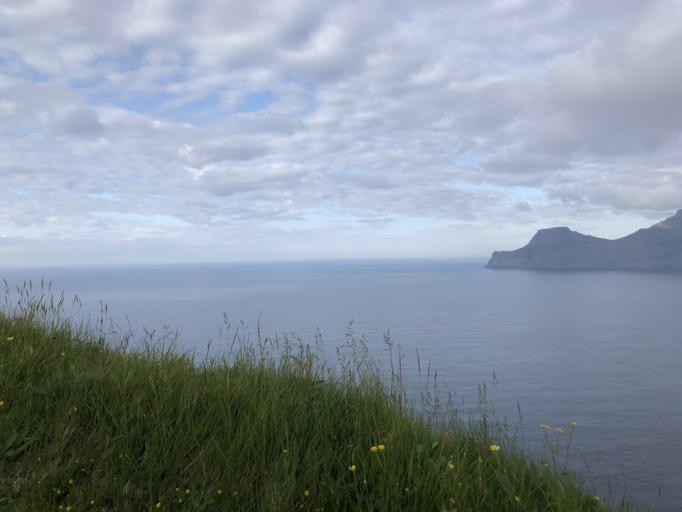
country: FO
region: Eysturoy
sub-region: Eidi
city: Eidi
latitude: 62.3299
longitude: -6.9504
